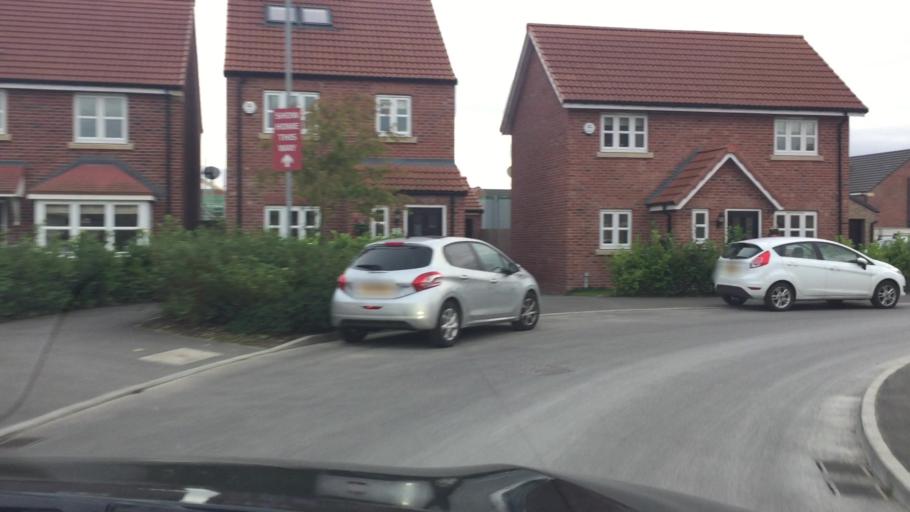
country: GB
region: England
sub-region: East Riding of Yorkshire
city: Pocklington
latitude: 53.9250
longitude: -0.7819
